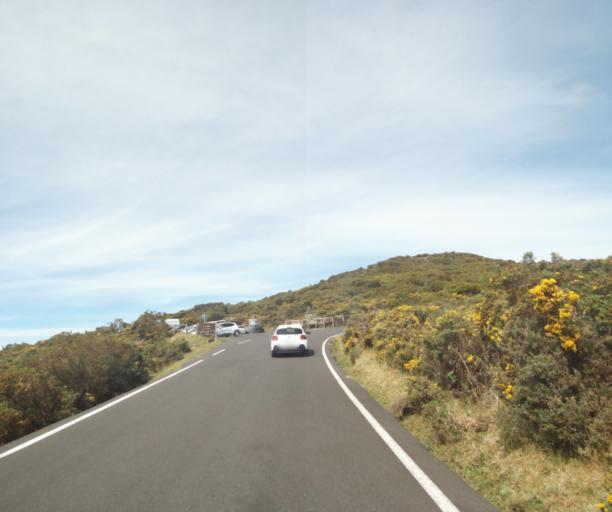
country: RE
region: Reunion
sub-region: Reunion
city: Trois-Bassins
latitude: -21.0695
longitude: 55.3848
